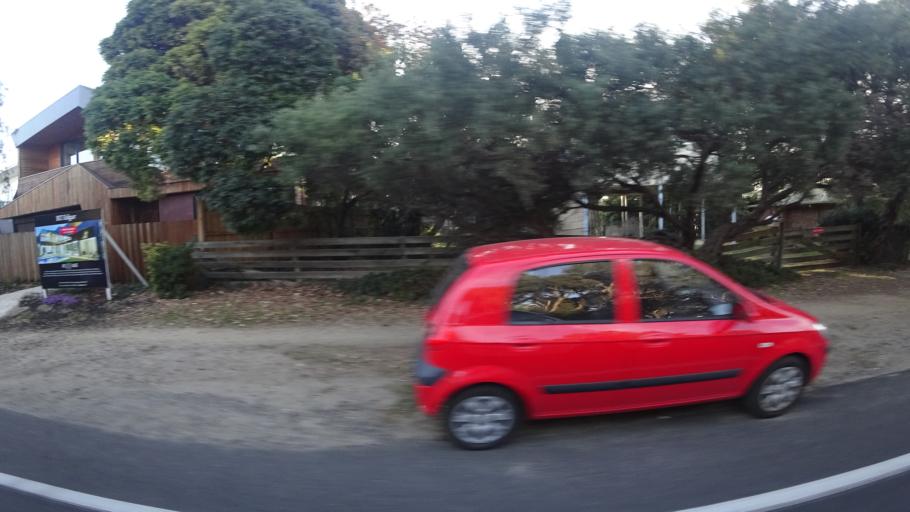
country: AU
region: Victoria
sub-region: Queenscliffe
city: Queenscliff
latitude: -38.2780
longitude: 144.6168
